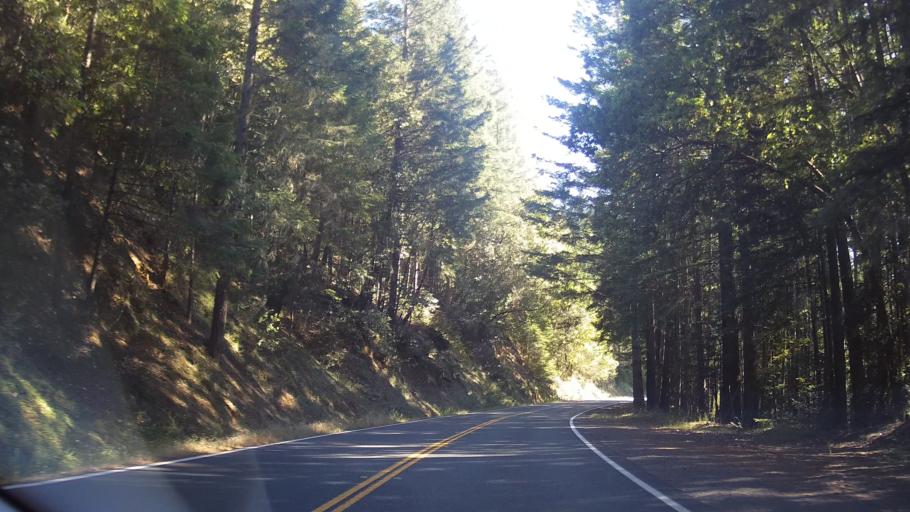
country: US
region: California
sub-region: Mendocino County
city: Brooktrails
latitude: 39.3871
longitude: -123.4688
